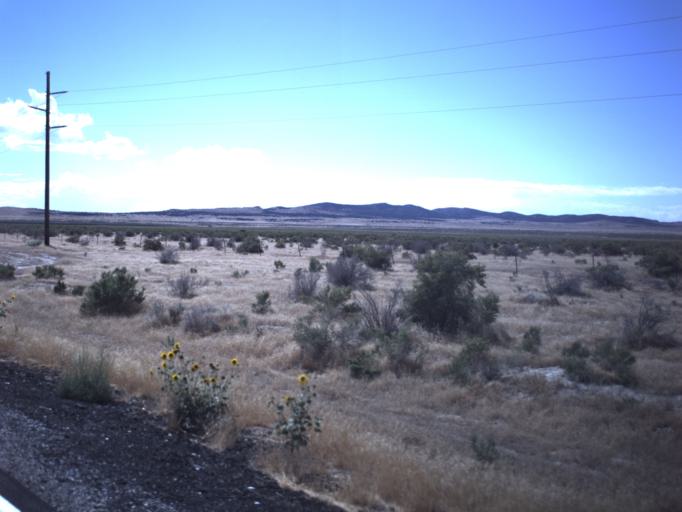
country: US
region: Utah
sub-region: Tooele County
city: Grantsville
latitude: 40.2682
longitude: -112.6841
